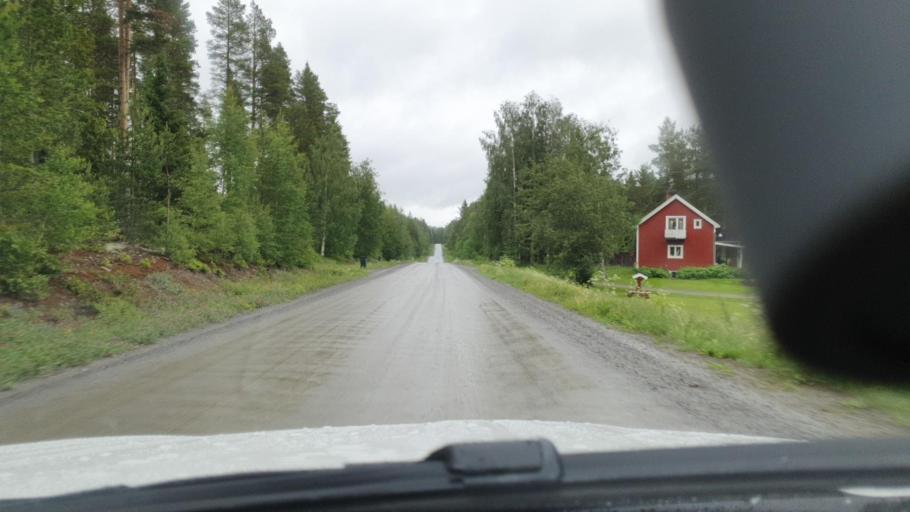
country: SE
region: Vaesterbotten
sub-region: Skelleftea Kommun
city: Burtraesk
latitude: 64.3693
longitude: 20.3854
